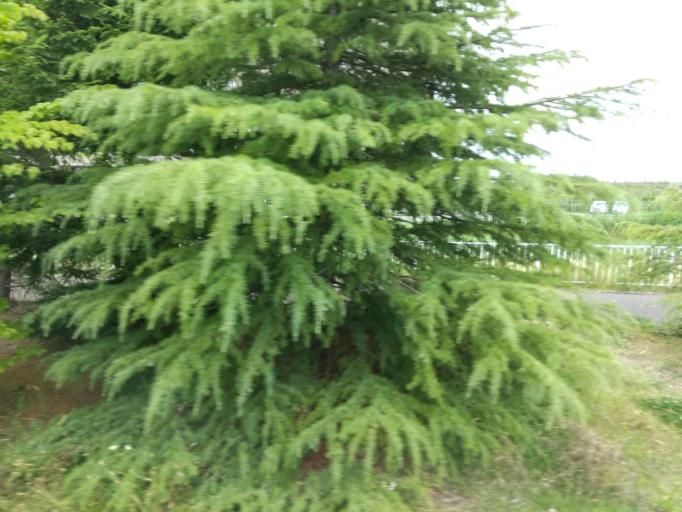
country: JP
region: Miyagi
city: Rifu
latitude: 38.2804
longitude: 140.9369
